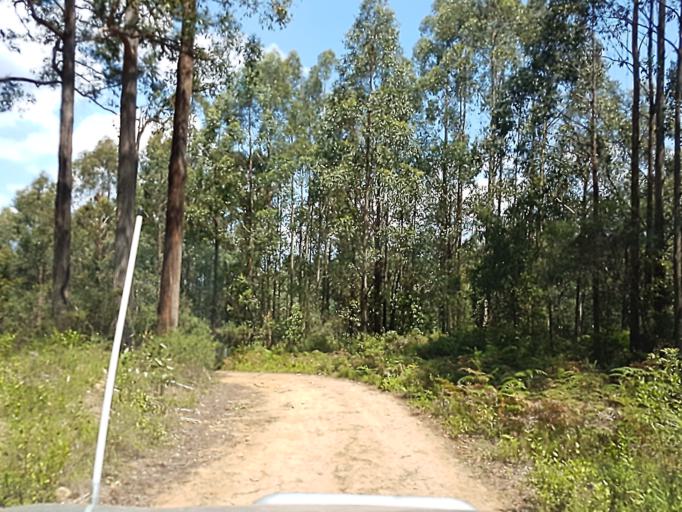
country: AU
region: Victoria
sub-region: East Gippsland
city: Lakes Entrance
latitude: -37.3939
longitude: 148.2957
